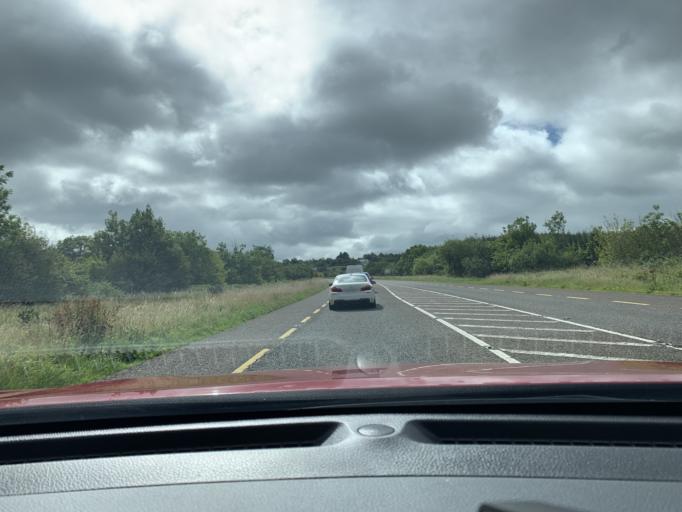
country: IE
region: Connaught
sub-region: Roscommon
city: Boyle
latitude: 54.0244
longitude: -8.3360
